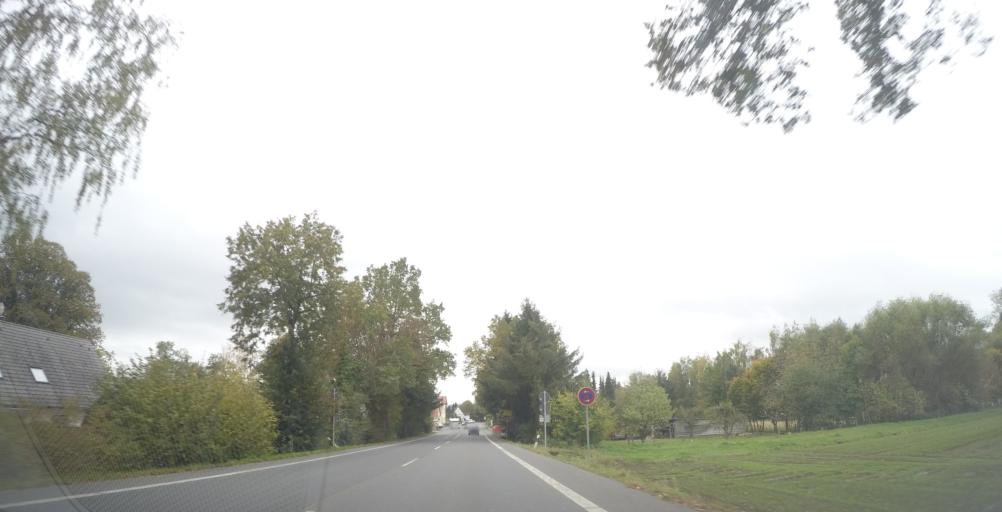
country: DE
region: North Rhine-Westphalia
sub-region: Regierungsbezirk Arnsberg
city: Unna
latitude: 51.4890
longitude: 7.7066
